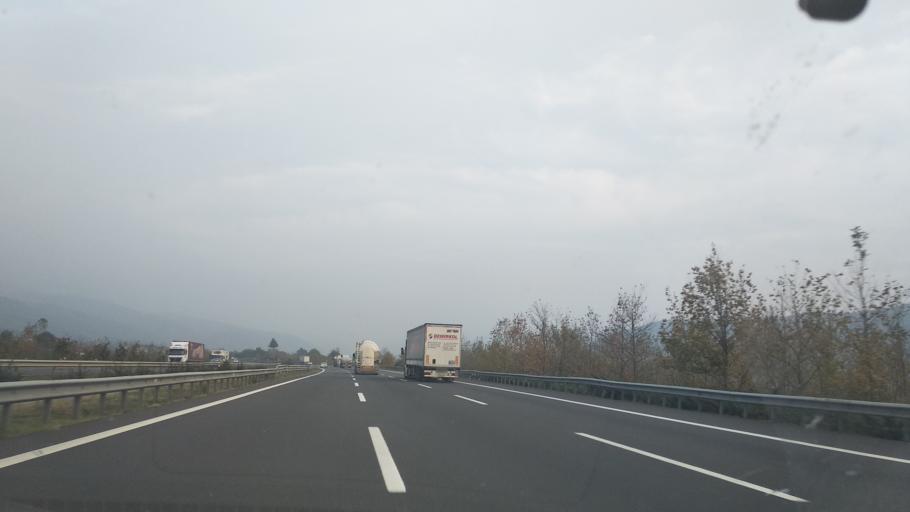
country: TR
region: Duzce
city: Kaynasli
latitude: 40.7807
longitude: 31.3211
